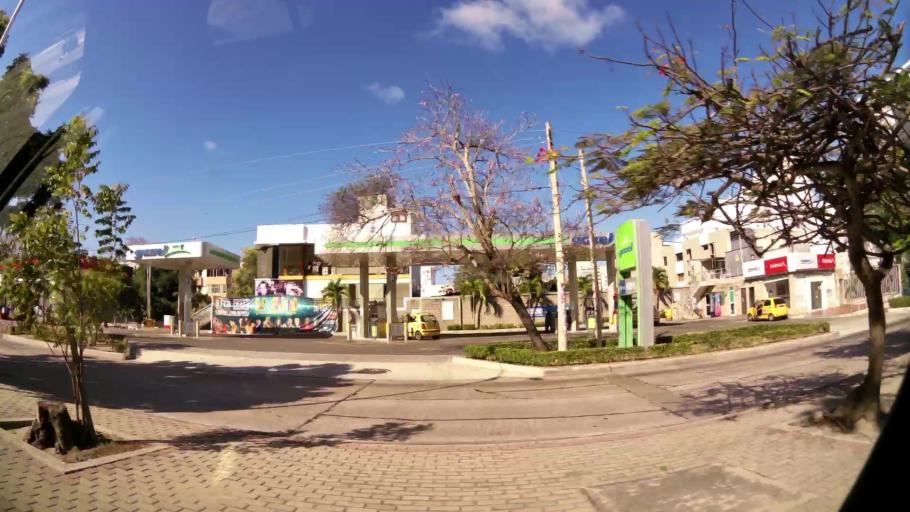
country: CO
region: Atlantico
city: Barranquilla
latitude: 11.0025
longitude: -74.8223
